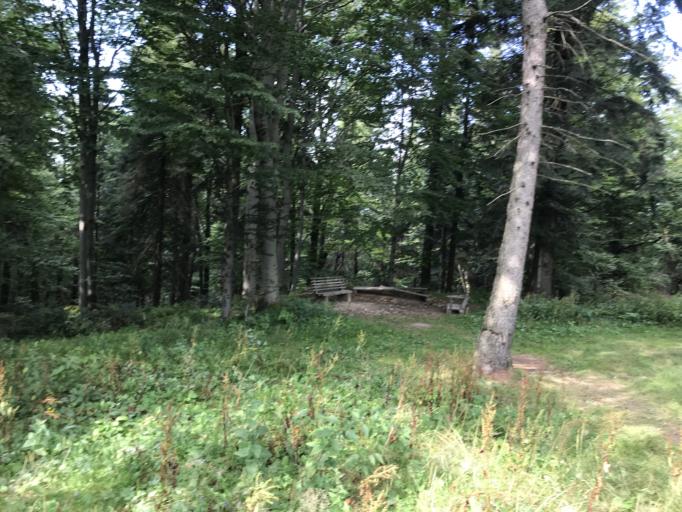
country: PL
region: Lesser Poland Voivodeship
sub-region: Powiat gorlicki
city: Uscie Gorlickie
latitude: 49.4749
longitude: 21.2354
